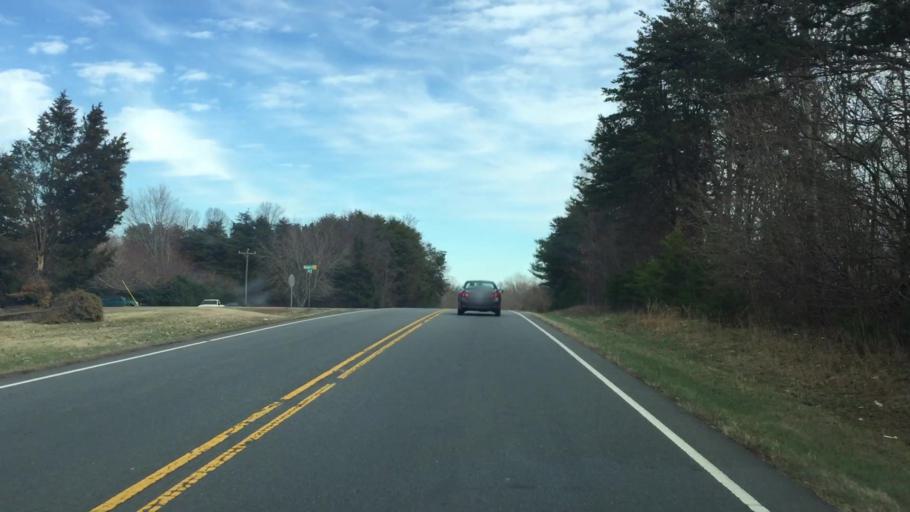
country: US
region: North Carolina
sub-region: Forsyth County
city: Walkertown
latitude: 36.1778
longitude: -80.1231
